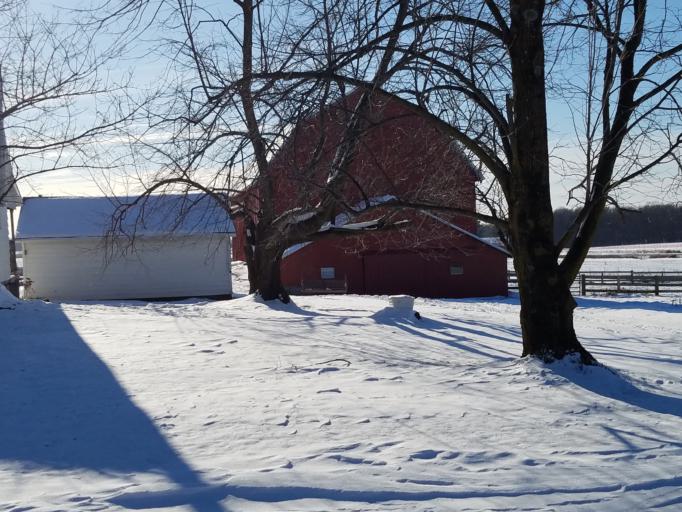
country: US
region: Wisconsin
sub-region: Clark County
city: Neillsville
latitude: 44.5676
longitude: -90.4530
